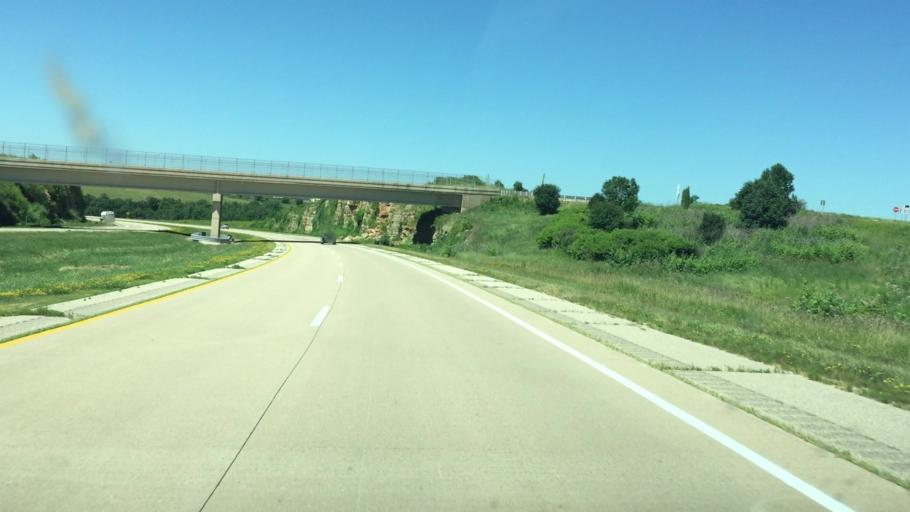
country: US
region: Wisconsin
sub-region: Iowa County
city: Mineral Point
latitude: 42.8473
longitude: -90.1985
